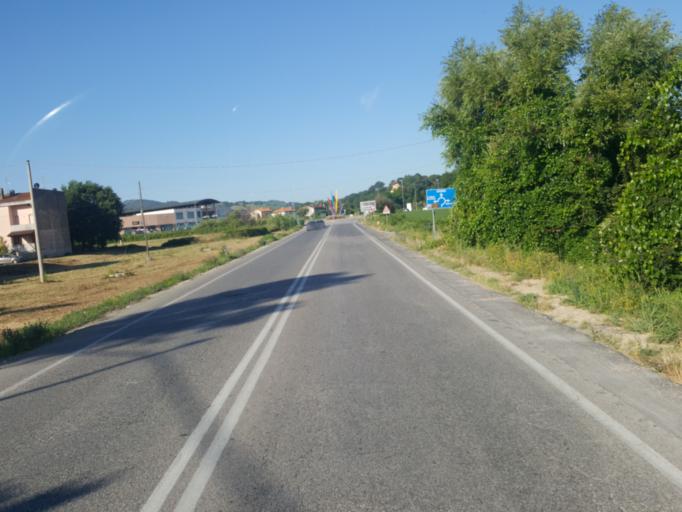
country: IT
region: The Marches
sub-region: Provincia di Pesaro e Urbino
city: Montelabbate
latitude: 43.8427
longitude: 12.7697
